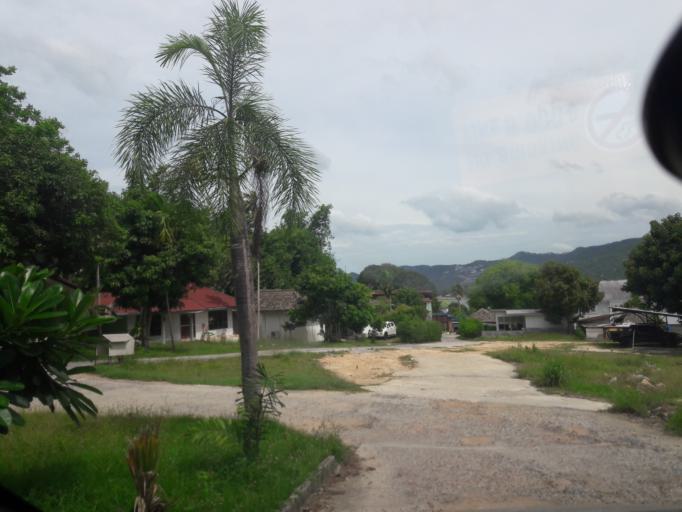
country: TH
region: Surat Thani
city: Ko Samui
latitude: 9.5377
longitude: 100.0552
